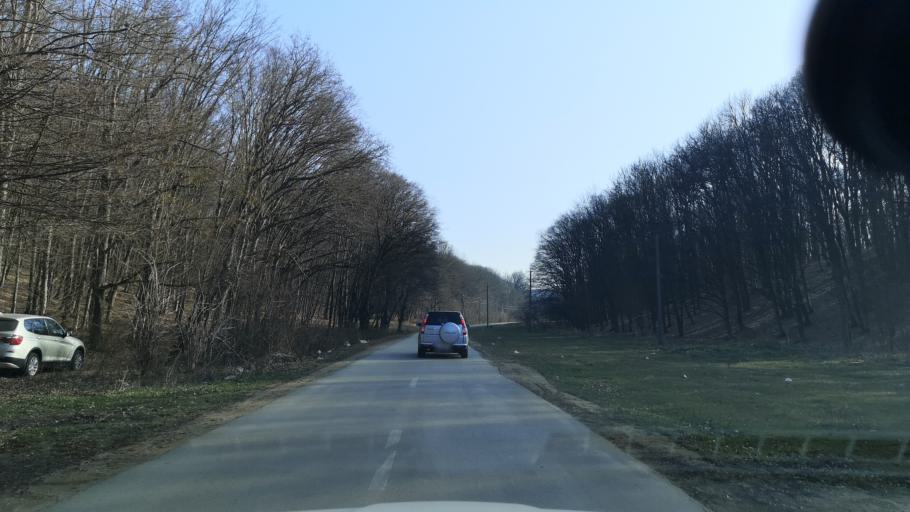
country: MD
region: Nisporeni
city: Nisporeni
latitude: 47.0871
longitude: 28.3191
